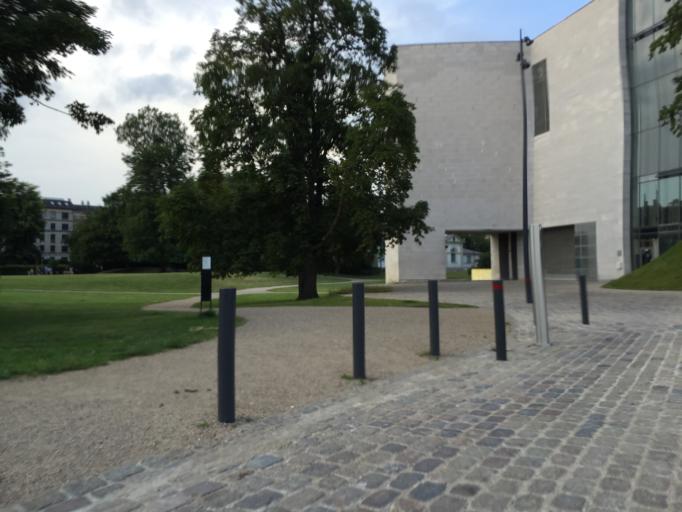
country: DK
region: Capital Region
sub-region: Kobenhavn
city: Copenhagen
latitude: 55.6885
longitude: 12.5768
